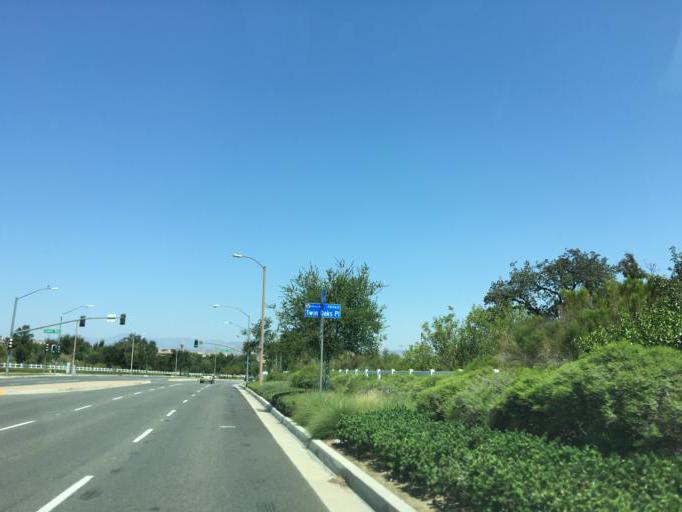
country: US
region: California
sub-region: Los Angeles County
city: Santa Clarita
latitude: 34.4048
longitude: -118.5779
